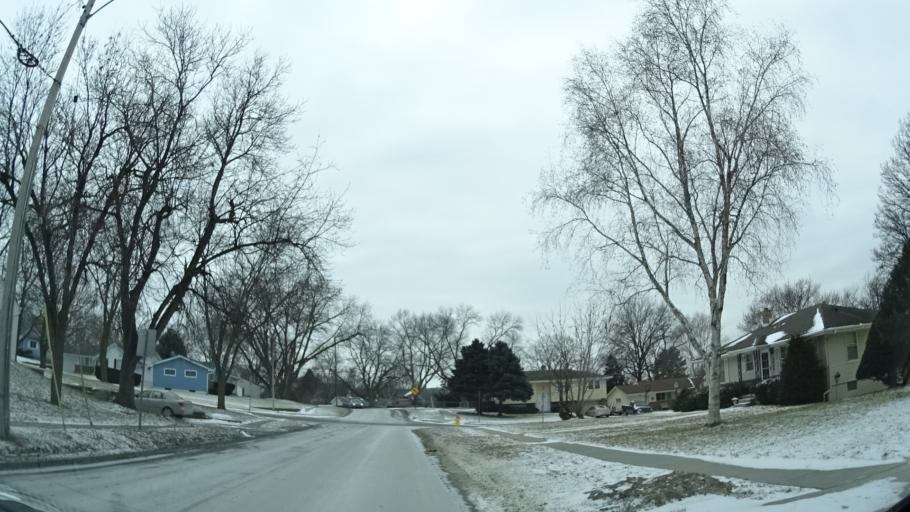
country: US
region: Nebraska
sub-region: Douglas County
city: Omaha
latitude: 41.2312
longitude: -95.9855
